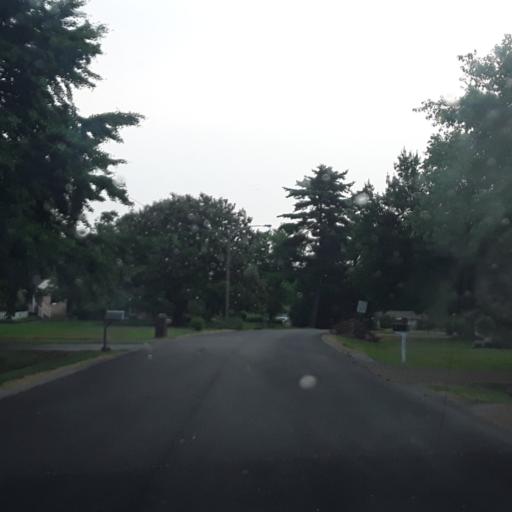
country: US
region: Tennessee
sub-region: Davidson County
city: Oak Hill
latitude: 36.0608
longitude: -86.7661
